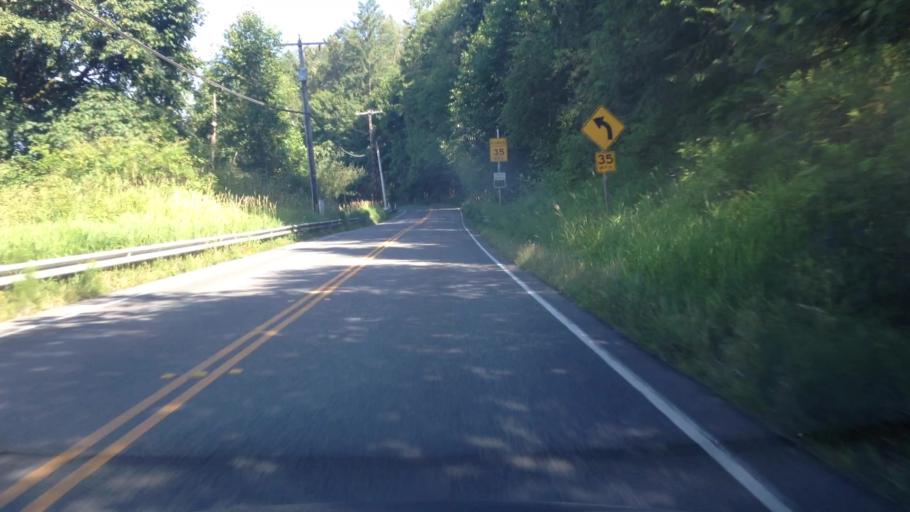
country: US
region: Washington
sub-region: King County
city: Duvall
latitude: 47.7435
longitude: -121.9494
